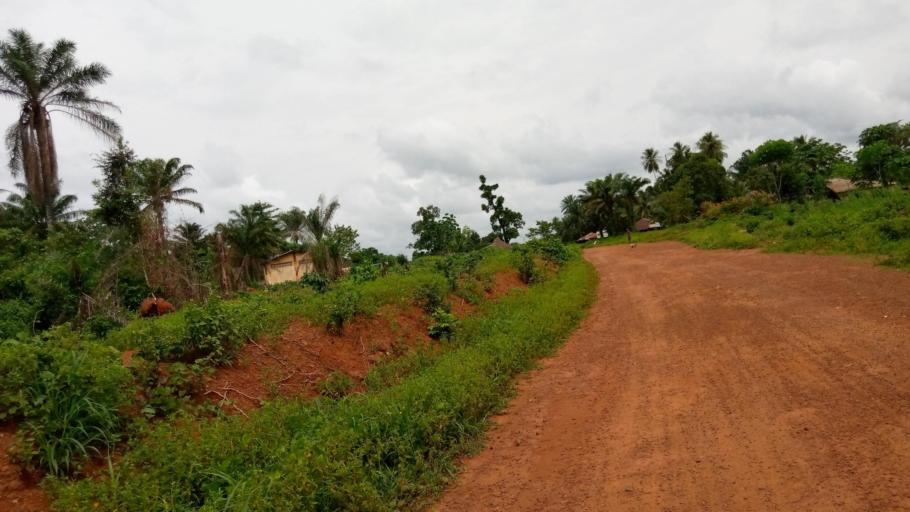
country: SL
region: Southern Province
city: Moyamba
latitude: 8.1749
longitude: -12.4994
